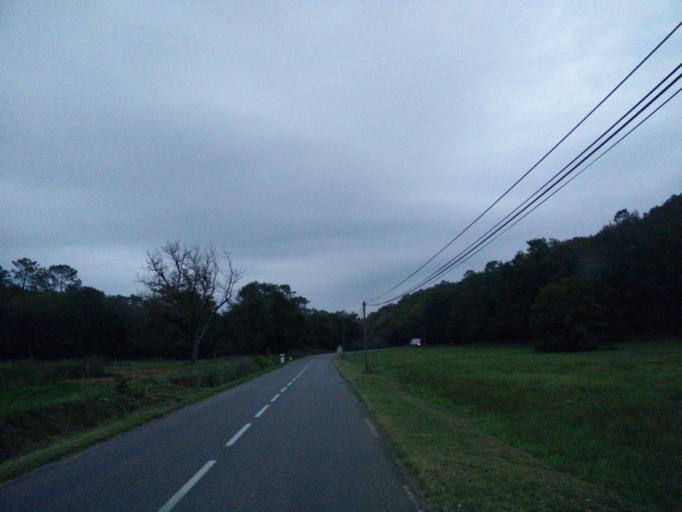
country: FR
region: Midi-Pyrenees
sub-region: Departement du Lot
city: Gourdon
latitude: 44.7741
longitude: 1.3342
